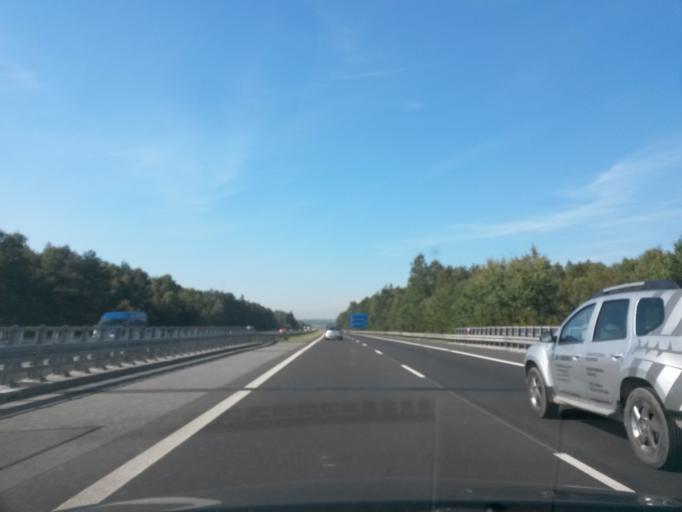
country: PL
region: Lesser Poland Voivodeship
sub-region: Powiat chrzanowski
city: Trzebinia
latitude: 50.1389
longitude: 19.4622
